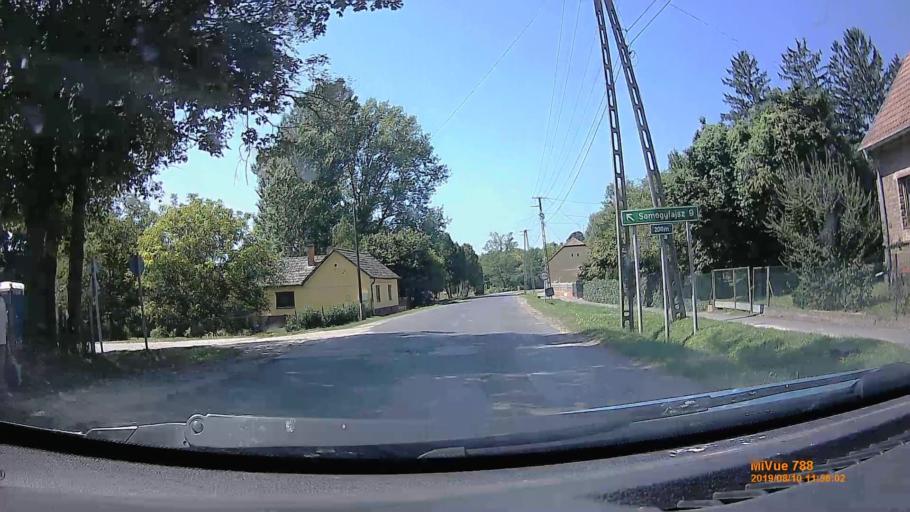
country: HU
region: Somogy
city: Somogyvar
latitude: 46.5196
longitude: 17.6725
